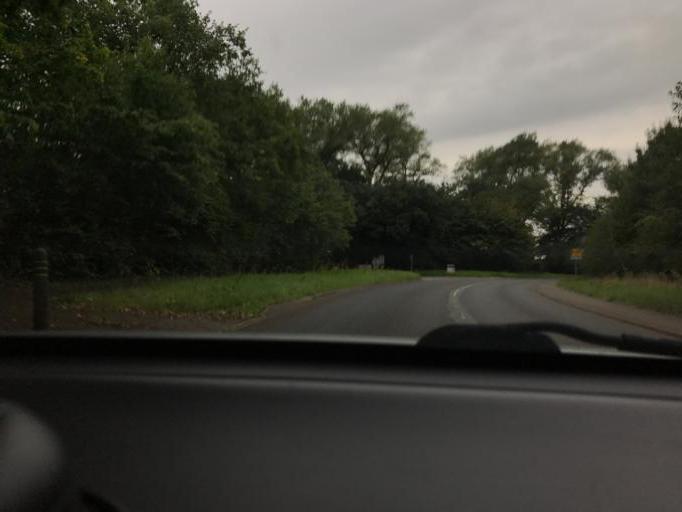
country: GB
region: England
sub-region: Cheshire West and Chester
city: Winsford
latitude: 53.2180
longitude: -2.5054
